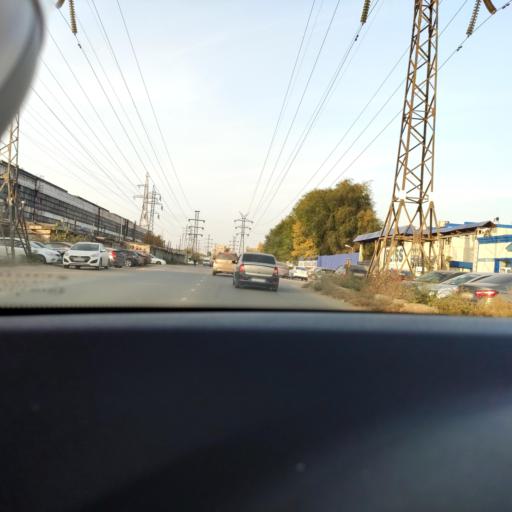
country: RU
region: Samara
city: Petra-Dubrava
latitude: 53.2408
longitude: 50.2894
